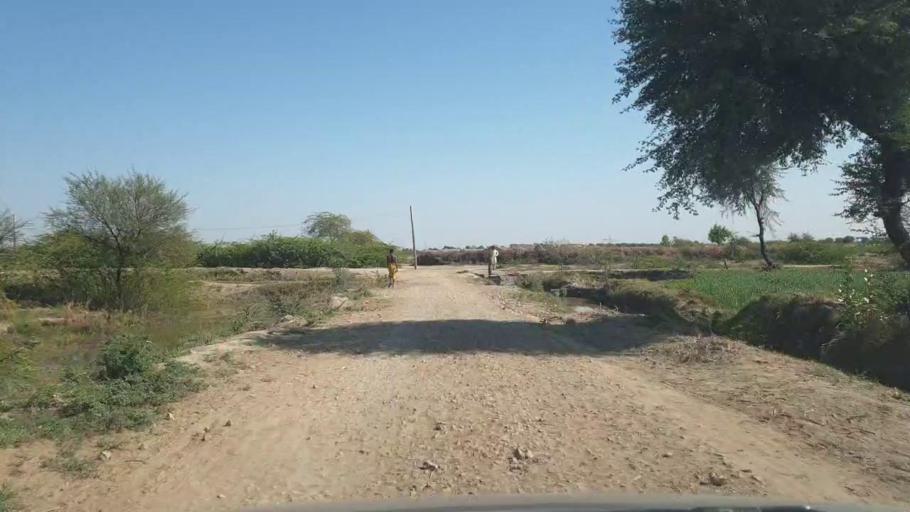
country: PK
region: Sindh
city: Dhoro Naro
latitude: 25.3791
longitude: 69.5992
